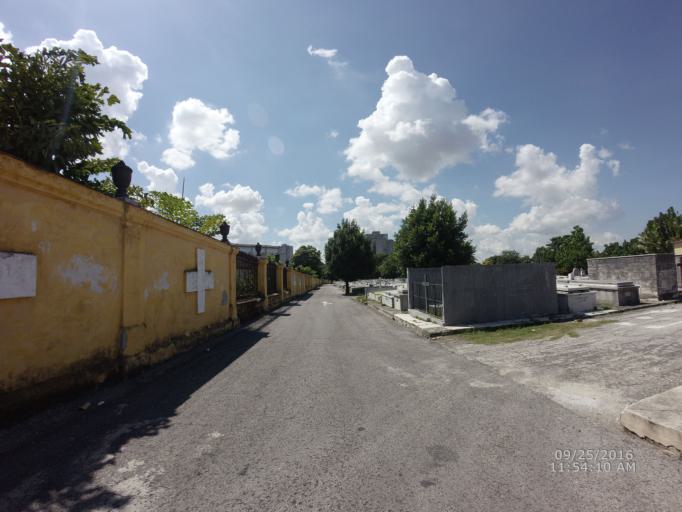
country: CU
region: La Habana
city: Havana
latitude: 23.1215
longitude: -82.3950
